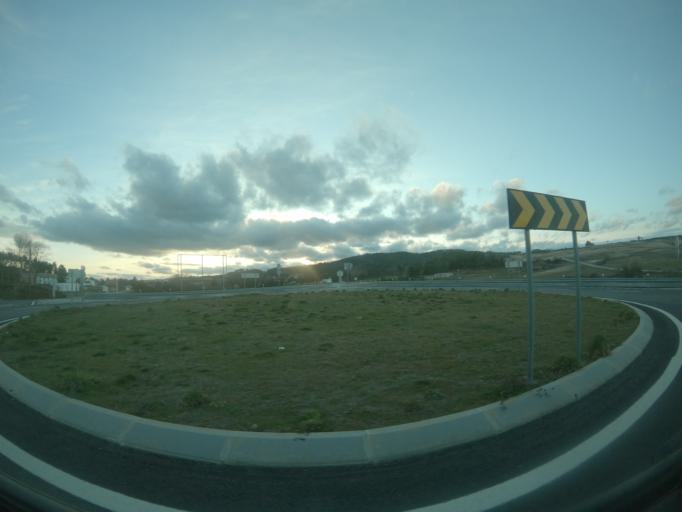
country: PT
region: Braganca
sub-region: Carrazeda de Ansiaes
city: Carrazeda de Anciaes
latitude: 41.2526
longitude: -7.2843
